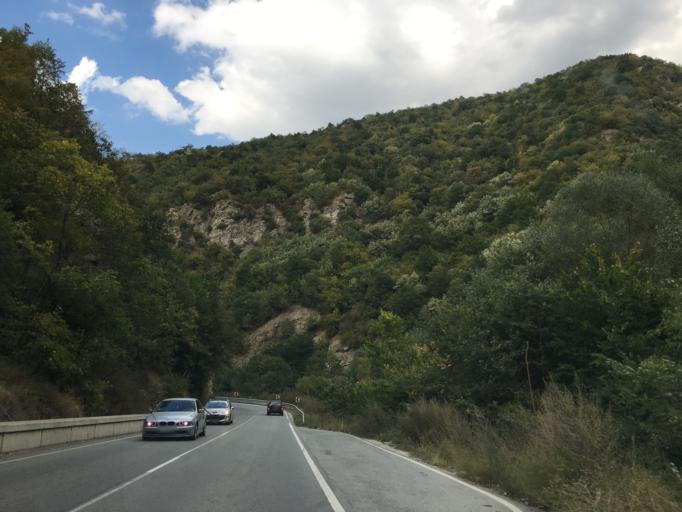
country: BG
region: Pazardzhik
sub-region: Obshtina Septemvri
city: Septemvri
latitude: 42.1234
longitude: 24.1231
